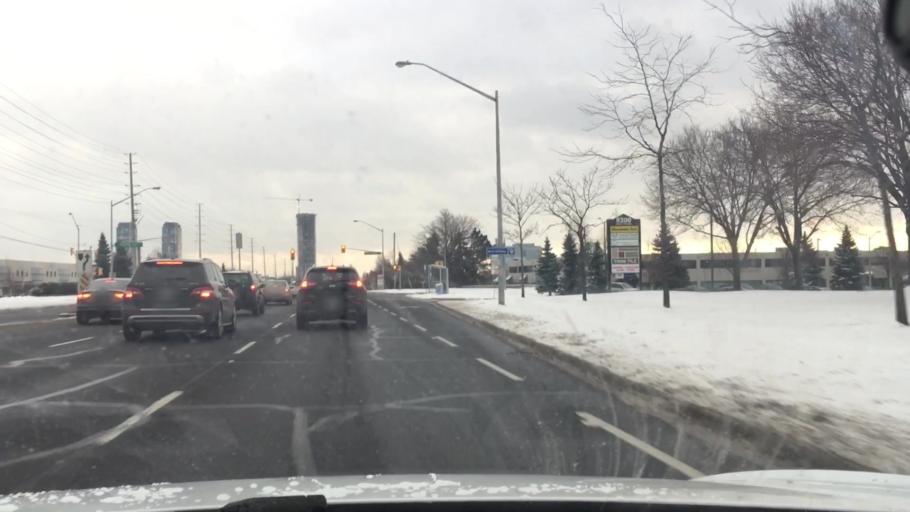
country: CA
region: Ontario
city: Vaughan
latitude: 43.8103
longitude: -79.5281
